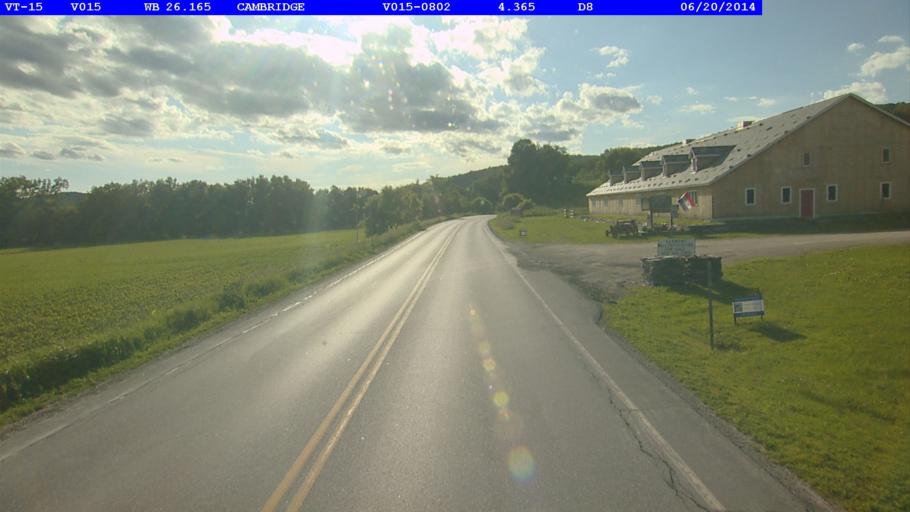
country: US
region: Vermont
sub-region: Lamoille County
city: Johnson
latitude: 44.6444
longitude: -72.8429
